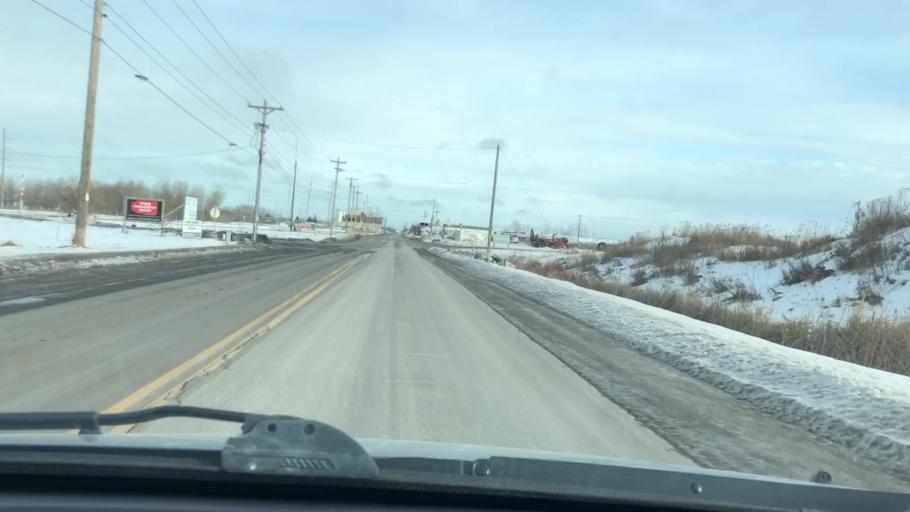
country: US
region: Wisconsin
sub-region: Douglas County
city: Superior
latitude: 46.7279
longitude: -92.1172
